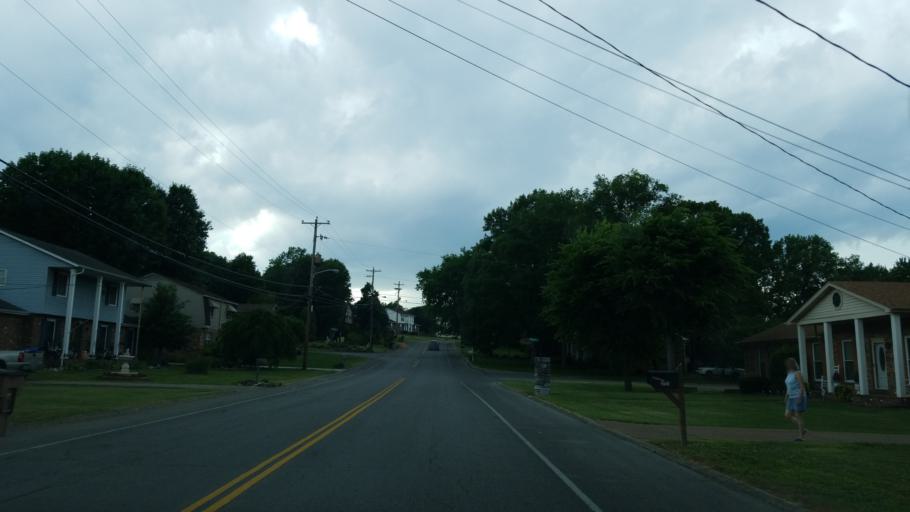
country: US
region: Tennessee
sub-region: Rutherford County
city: La Vergne
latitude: 36.0915
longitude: -86.6082
